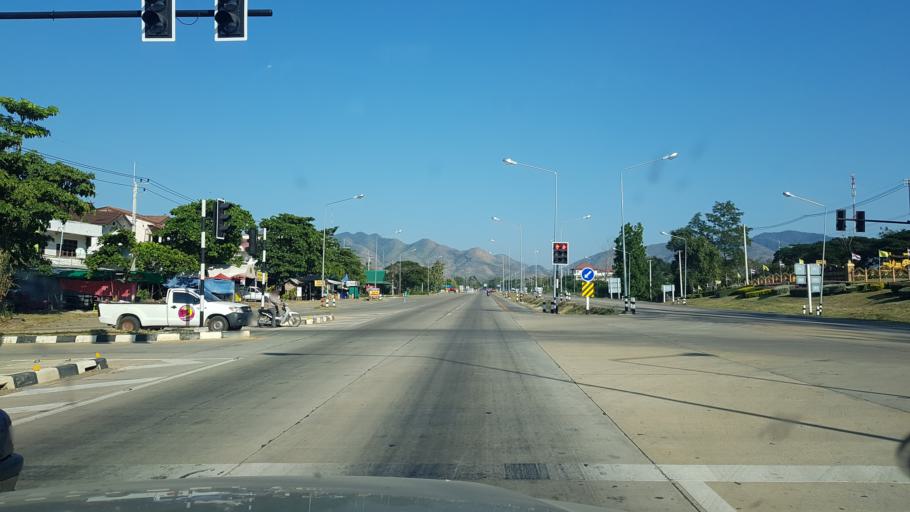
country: TH
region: Phetchabun
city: Lom Sak
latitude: 16.7284
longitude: 101.2849
